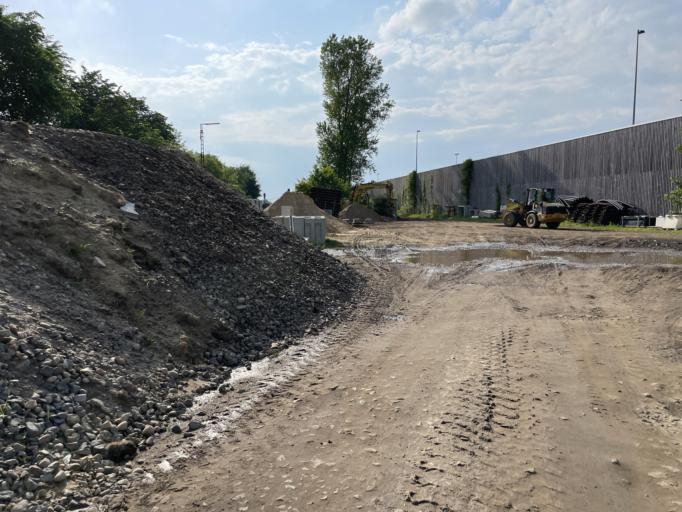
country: DE
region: Schleswig-Holstein
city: Husum
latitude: 54.4711
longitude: 9.0636
